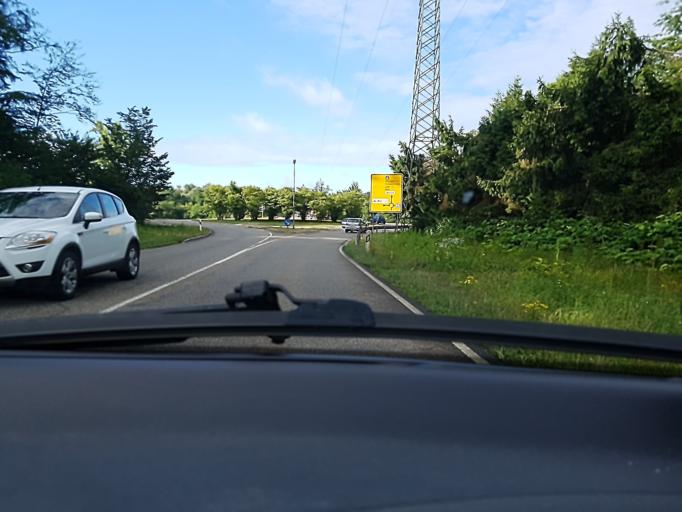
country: DE
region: Baden-Wuerttemberg
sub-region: Freiburg Region
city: Offenburg
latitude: 48.4727
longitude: 7.9210
